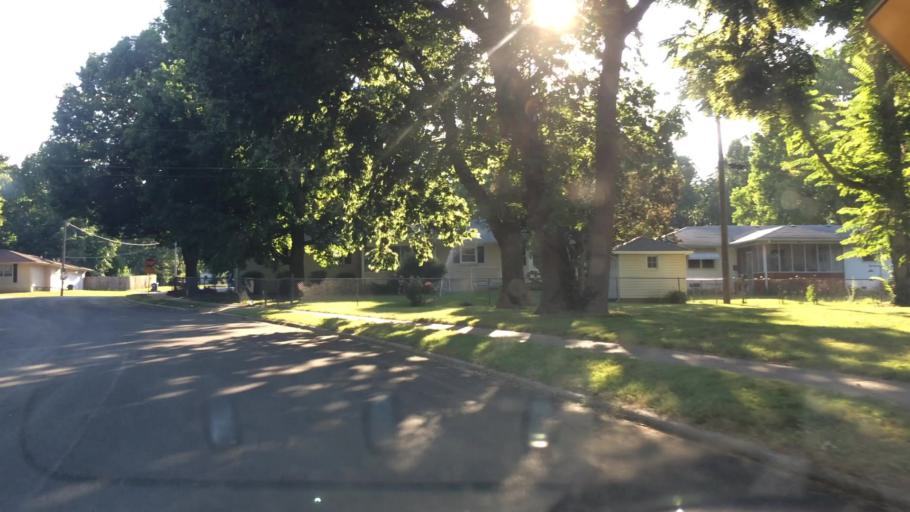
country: US
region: Missouri
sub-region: Greene County
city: Springfield
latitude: 37.2015
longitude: -93.2557
